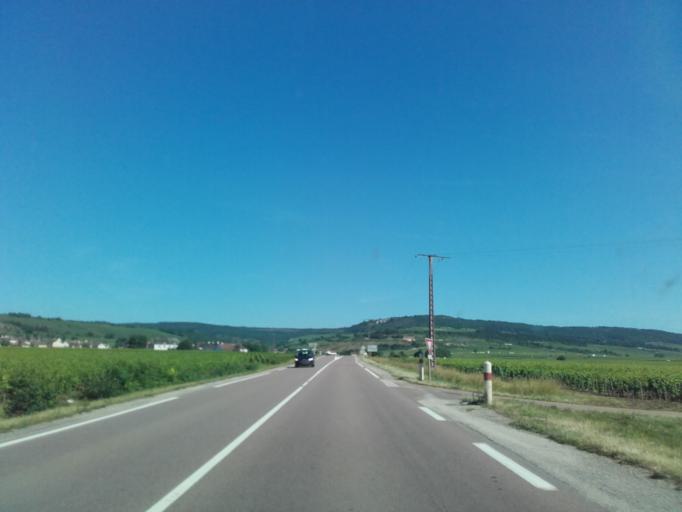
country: FR
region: Bourgogne
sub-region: Departement de la Cote-d'Or
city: Corpeau
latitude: 46.9319
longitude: 4.7402
